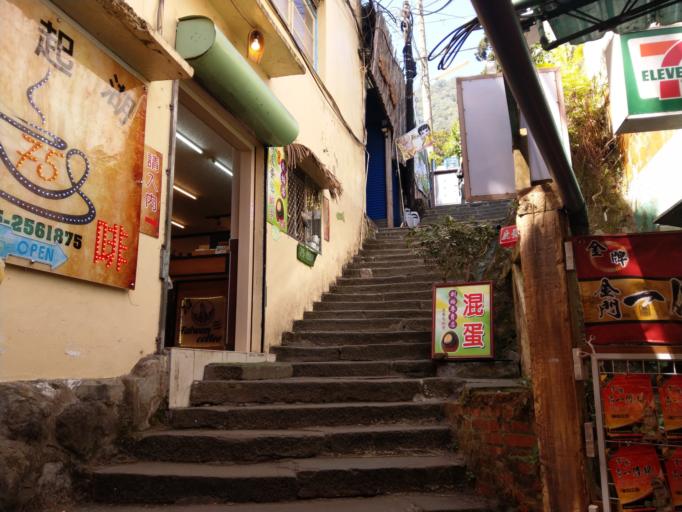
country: TW
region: Taiwan
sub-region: Chiayi
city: Jiayi Shi
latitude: 23.5051
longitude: 120.6952
